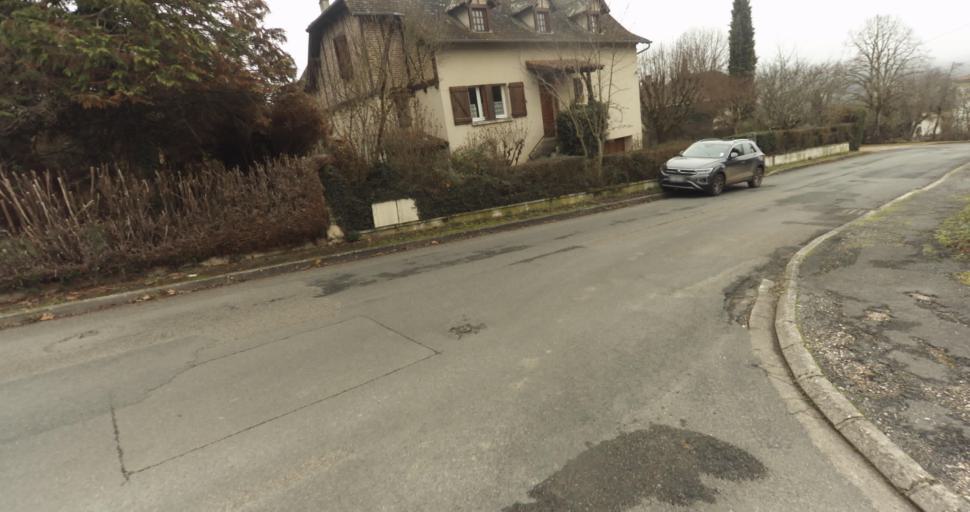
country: FR
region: Midi-Pyrenees
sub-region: Departement du Lot
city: Figeac
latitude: 44.6135
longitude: 2.0440
